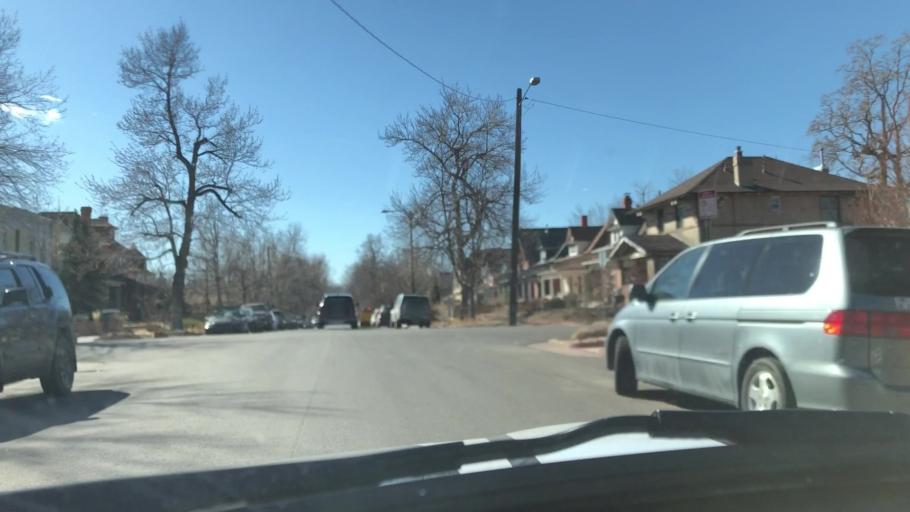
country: US
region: Colorado
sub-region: Denver County
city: Denver
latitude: 39.7534
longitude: -104.9648
